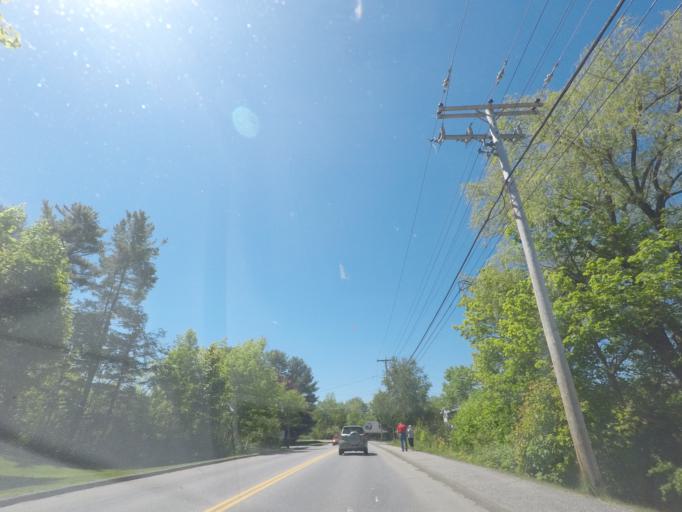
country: US
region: Maine
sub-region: Kennebec County
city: Augusta
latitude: 44.3180
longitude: -69.8027
